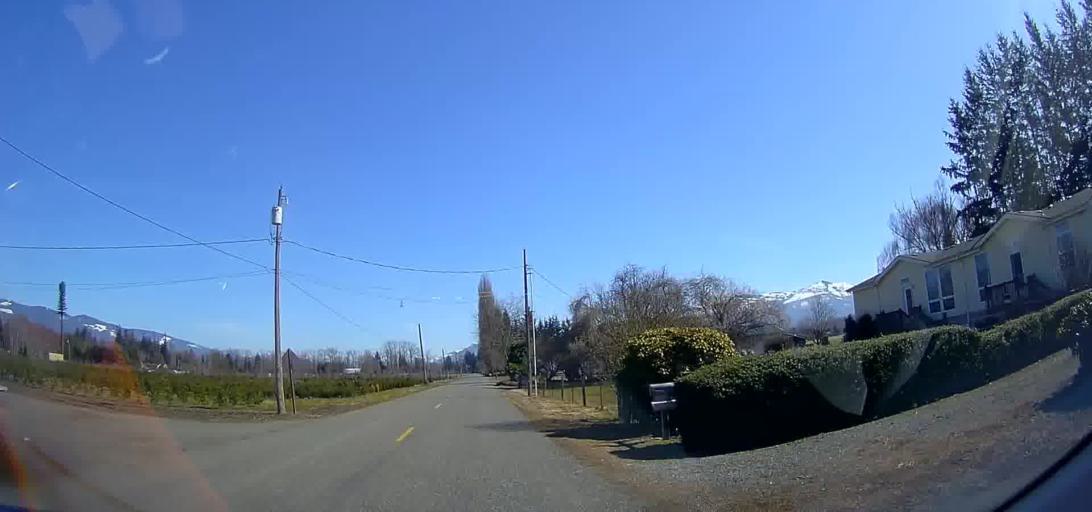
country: US
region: Washington
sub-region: Skagit County
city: Burlington
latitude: 48.4893
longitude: -122.2851
